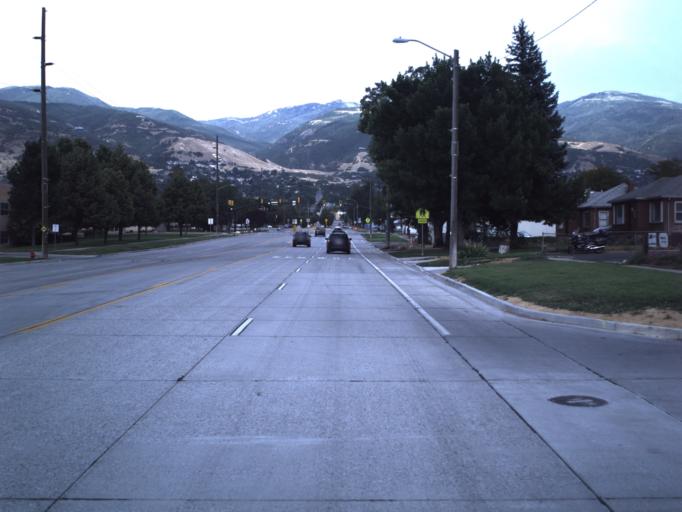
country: US
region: Utah
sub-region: Davis County
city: Bountiful
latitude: 40.8936
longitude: -111.8830
